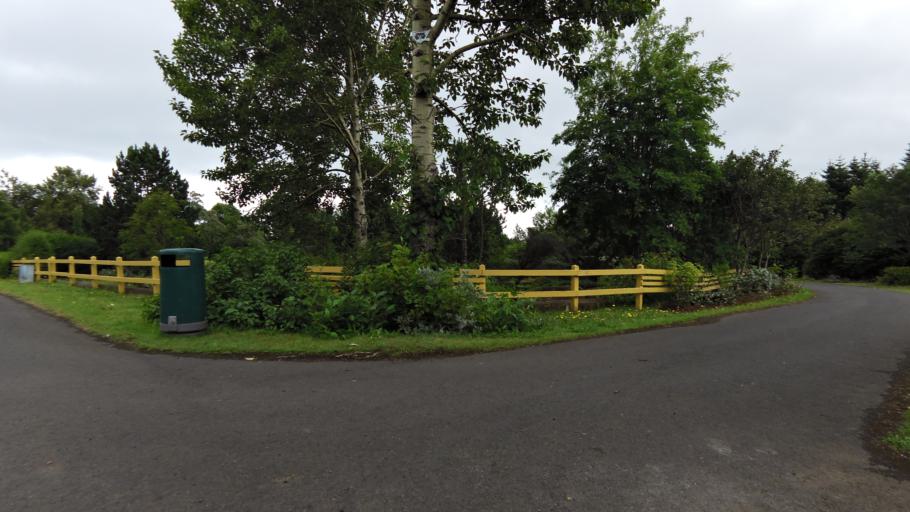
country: IS
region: Capital Region
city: Reykjavik
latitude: 64.1367
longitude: -21.8689
